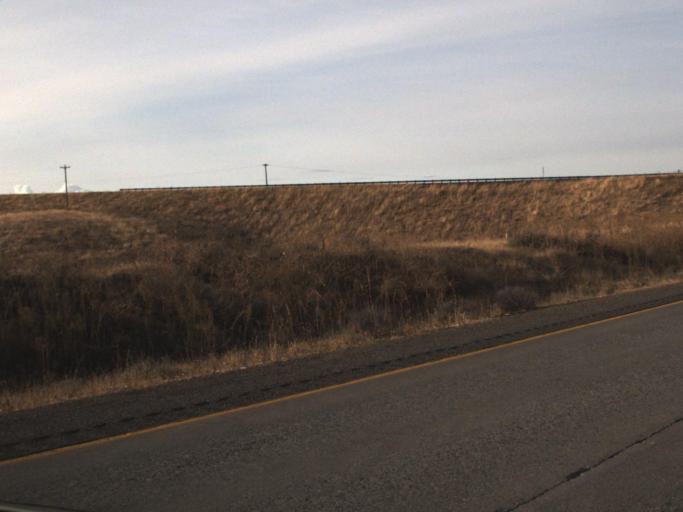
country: US
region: Washington
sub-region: Benton County
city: Highland
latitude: 46.0611
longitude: -119.2234
